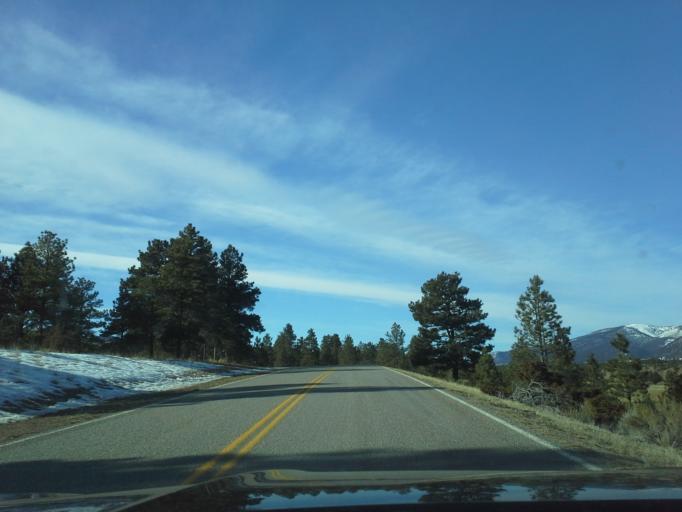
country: US
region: Montana
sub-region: Lewis and Clark County
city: Helena Valley Northeast
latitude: 46.8223
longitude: -111.9758
